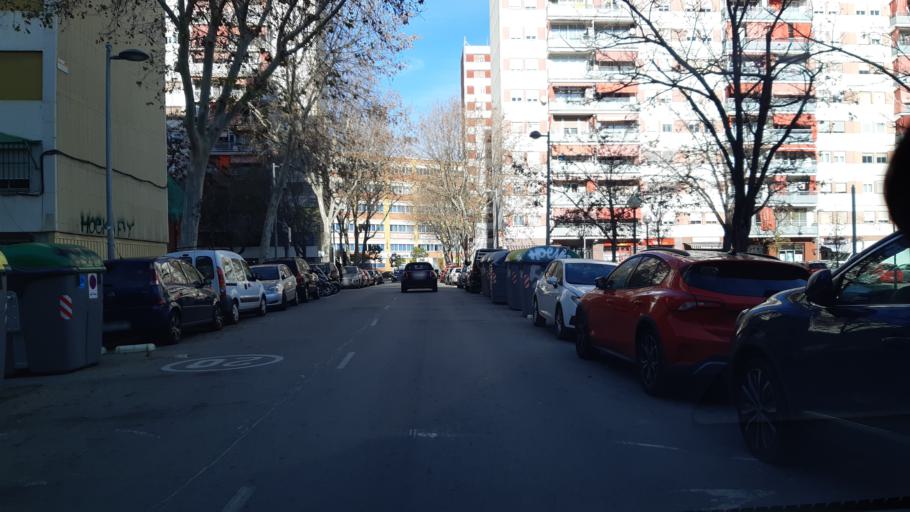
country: ES
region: Catalonia
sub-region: Provincia de Barcelona
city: L'Hospitalet de Llobregat
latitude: 41.3539
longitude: 2.1105
